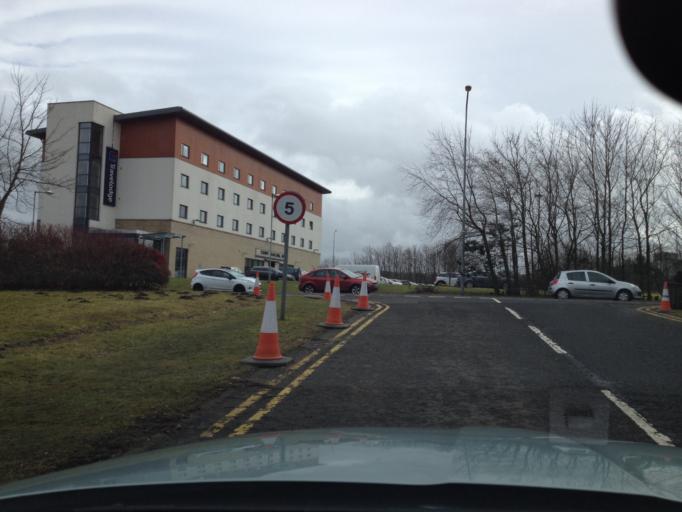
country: GB
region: Scotland
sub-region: West Lothian
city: Livingston
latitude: 55.8828
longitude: -3.5262
